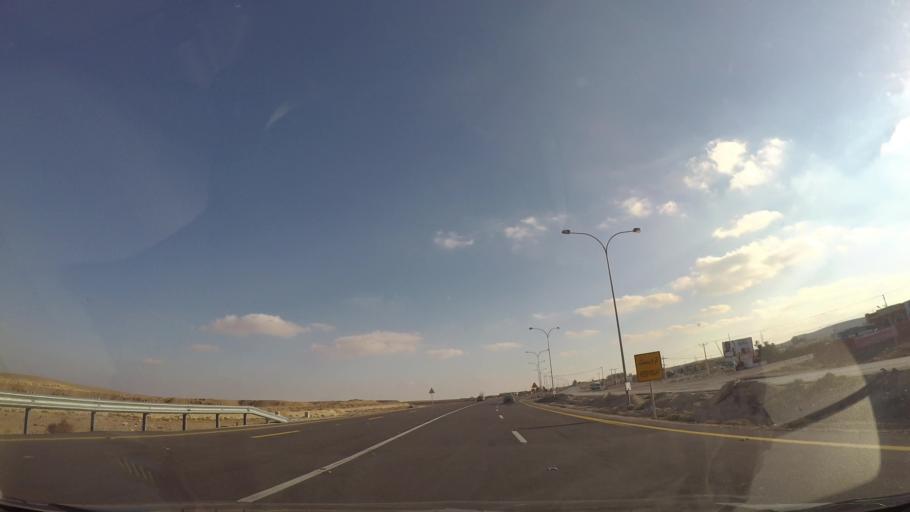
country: JO
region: Karak
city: Karak City
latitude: 31.0935
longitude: 36.0080
